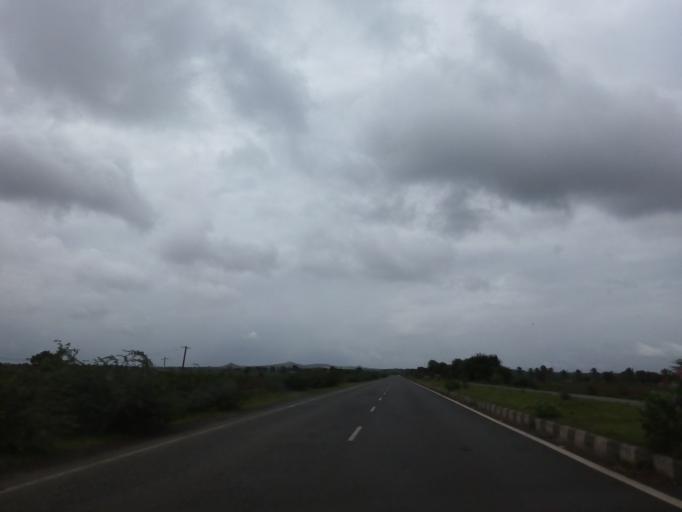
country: IN
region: Karnataka
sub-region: Haveri
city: Byadgi
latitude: 14.7407
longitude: 75.4592
